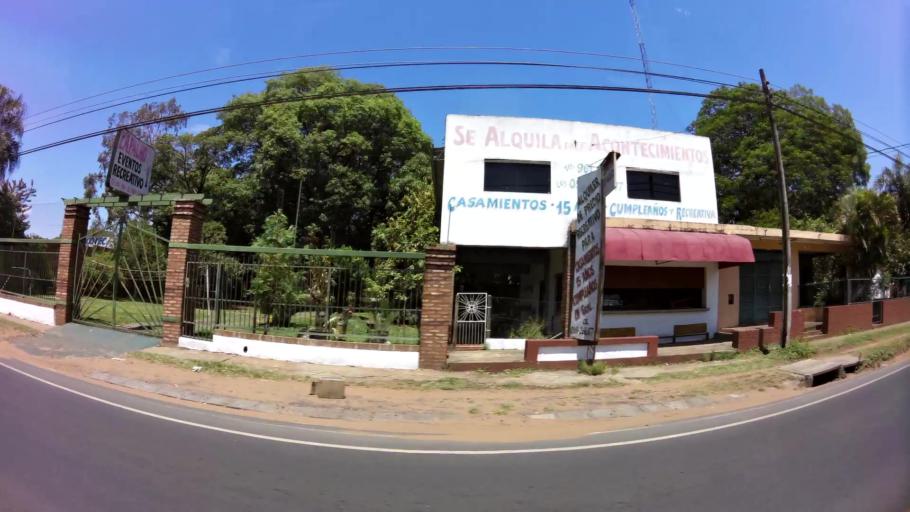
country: PY
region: Central
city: Nemby
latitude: -25.3972
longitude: -57.5372
